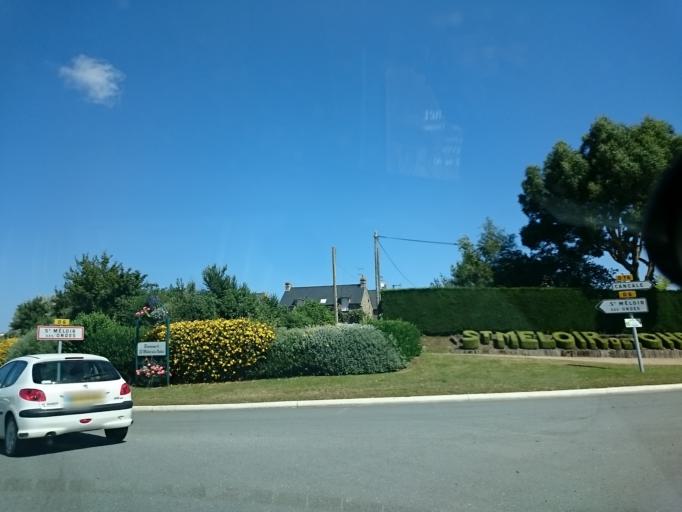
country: FR
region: Brittany
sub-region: Departement d'Ille-et-Vilaine
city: Saint-Meloir-des-Ondes
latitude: 48.6349
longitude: -1.8981
